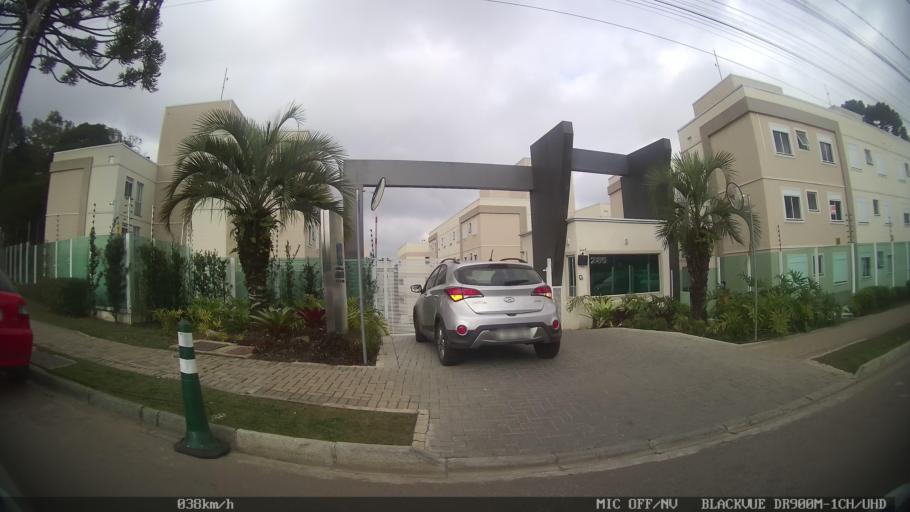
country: BR
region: Parana
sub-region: Curitiba
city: Curitiba
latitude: -25.3738
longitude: -49.2258
